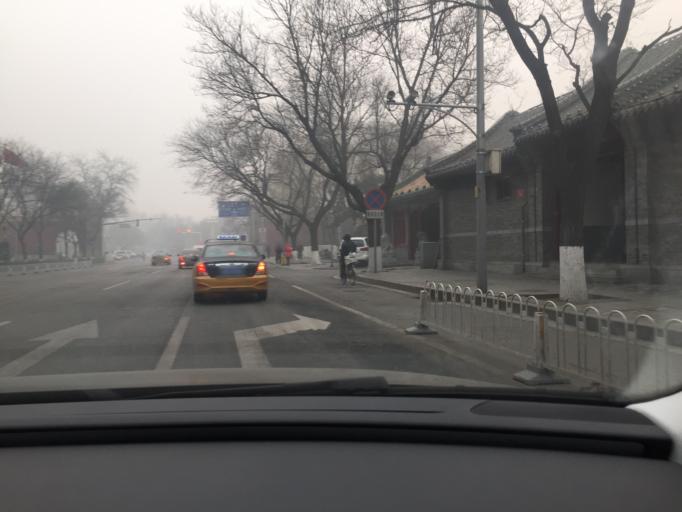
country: CN
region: Beijing
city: Beijing
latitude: 39.9079
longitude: 116.4005
